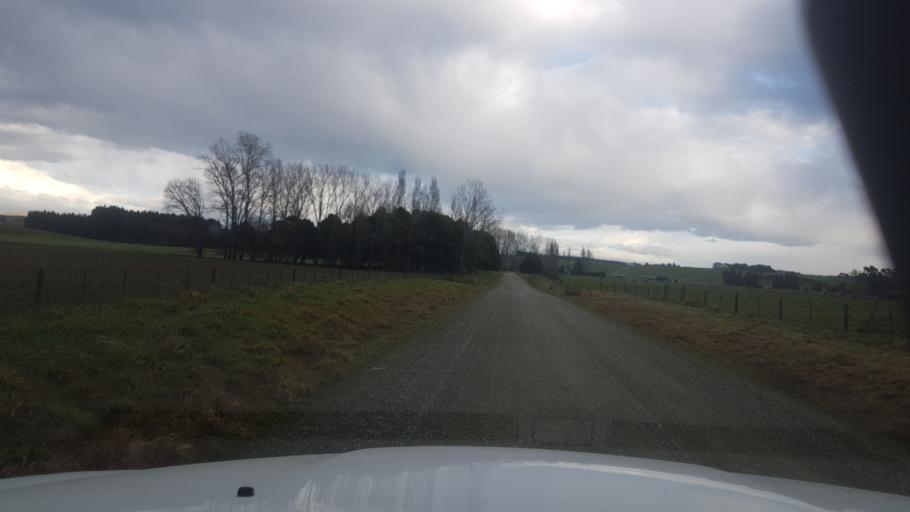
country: NZ
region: Canterbury
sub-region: Timaru District
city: Timaru
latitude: -44.3391
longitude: 171.1933
